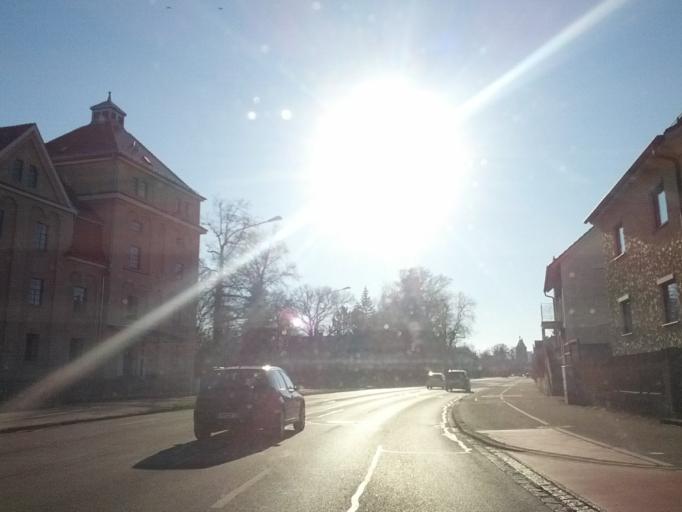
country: DE
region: Bavaria
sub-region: Swabia
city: Memmingen
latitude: 47.9939
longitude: 10.1801
